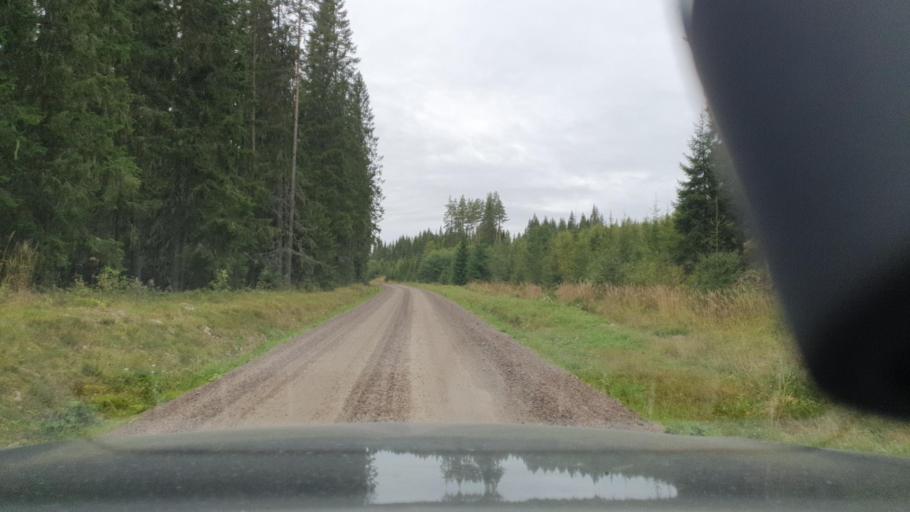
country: SE
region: Vaermland
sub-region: Eda Kommun
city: Charlottenberg
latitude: 60.0365
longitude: 12.5916
